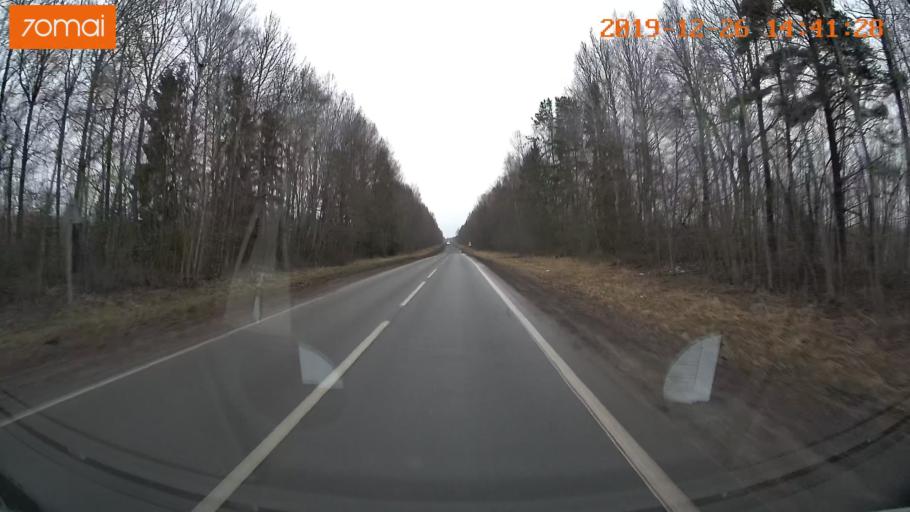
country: RU
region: Jaroslavl
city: Poshekhon'ye
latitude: 58.3711
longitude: 39.0195
